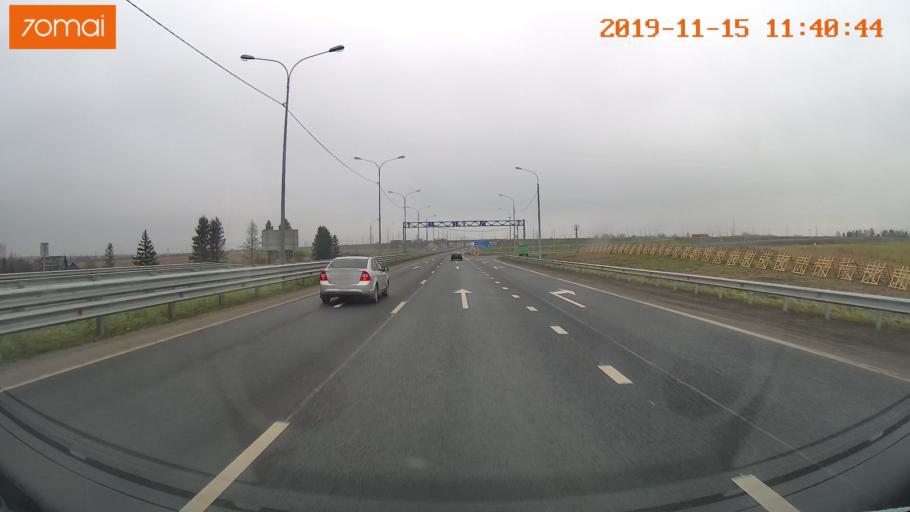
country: RU
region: Vologda
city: Molochnoye
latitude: 59.2128
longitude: 39.7588
